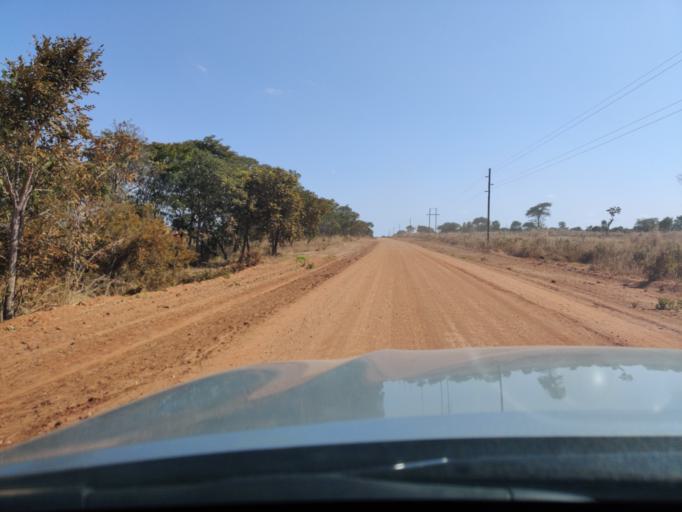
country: ZM
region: Central
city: Mkushi
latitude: -13.9910
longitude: 29.5305
